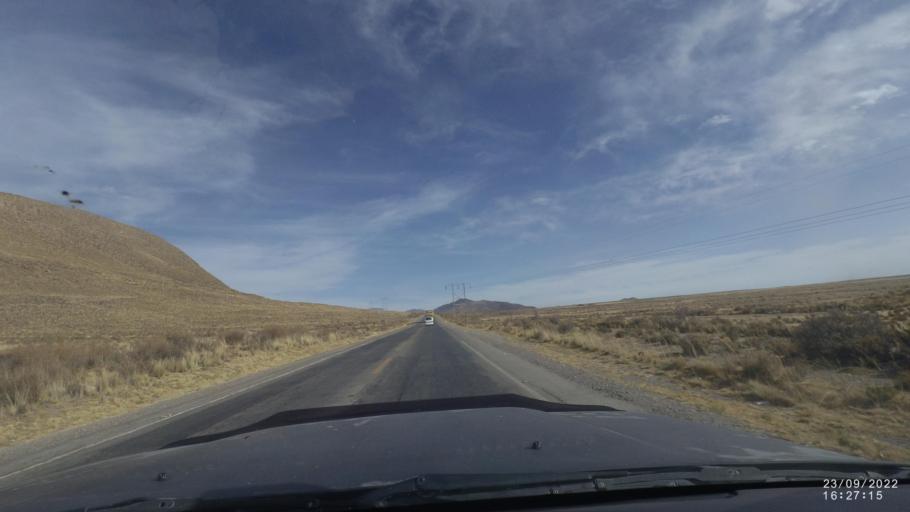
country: BO
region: Oruro
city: Machacamarca
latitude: -18.1153
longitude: -67.0040
